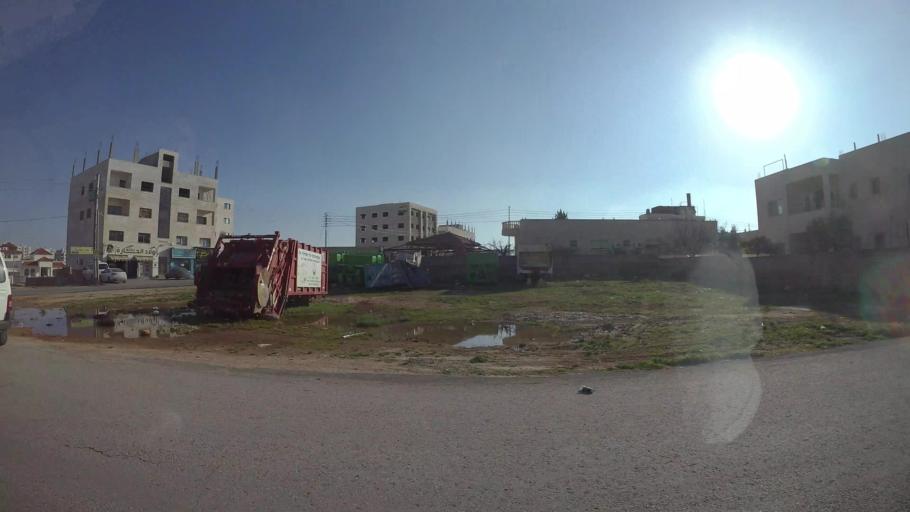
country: JO
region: Amman
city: Al Quwaysimah
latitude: 31.9018
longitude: 35.9232
